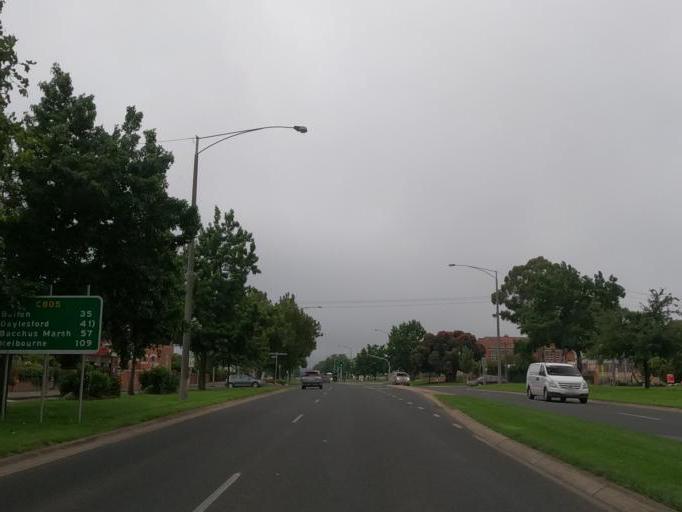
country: AU
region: Victoria
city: Ballarat East
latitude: -37.5616
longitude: 143.8721
